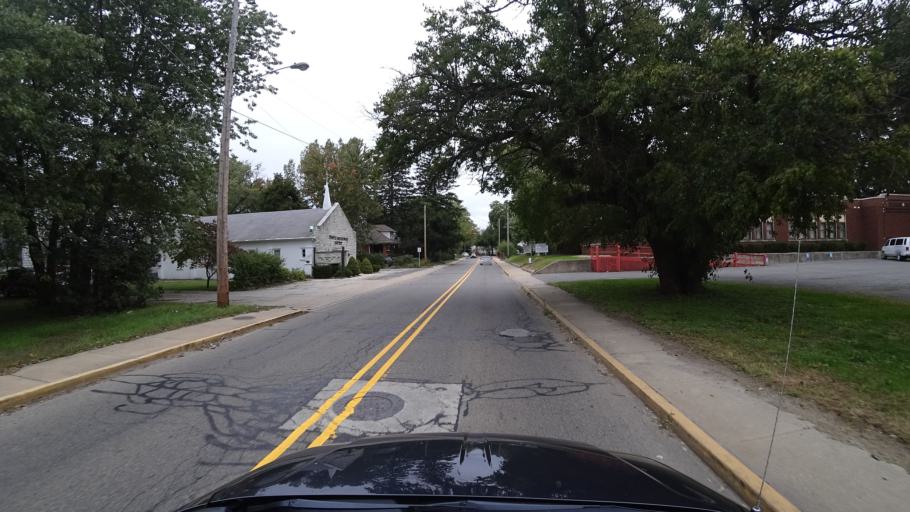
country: US
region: Indiana
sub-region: LaPorte County
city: Michigan City
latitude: 41.6967
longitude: -86.8956
